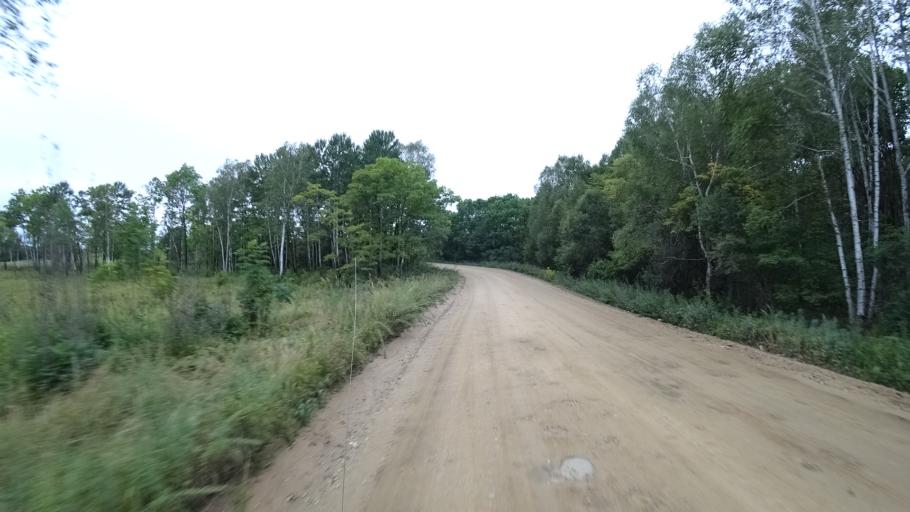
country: RU
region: Primorskiy
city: Rettikhovka
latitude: 44.1813
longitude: 132.8720
